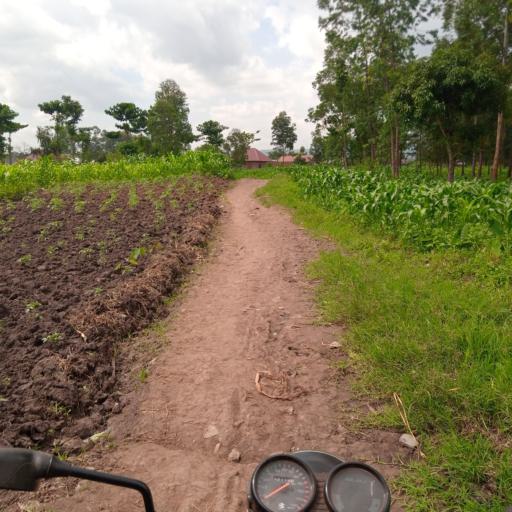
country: UG
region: Eastern Region
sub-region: Mbale District
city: Mbale
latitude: 1.1040
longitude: 34.1783
